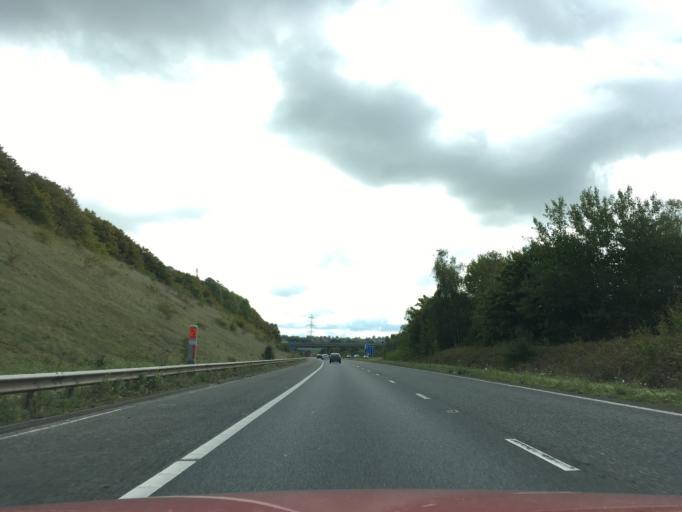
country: GB
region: England
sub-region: South Gloucestershire
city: Almondsbury
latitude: 51.5736
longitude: -2.5837
